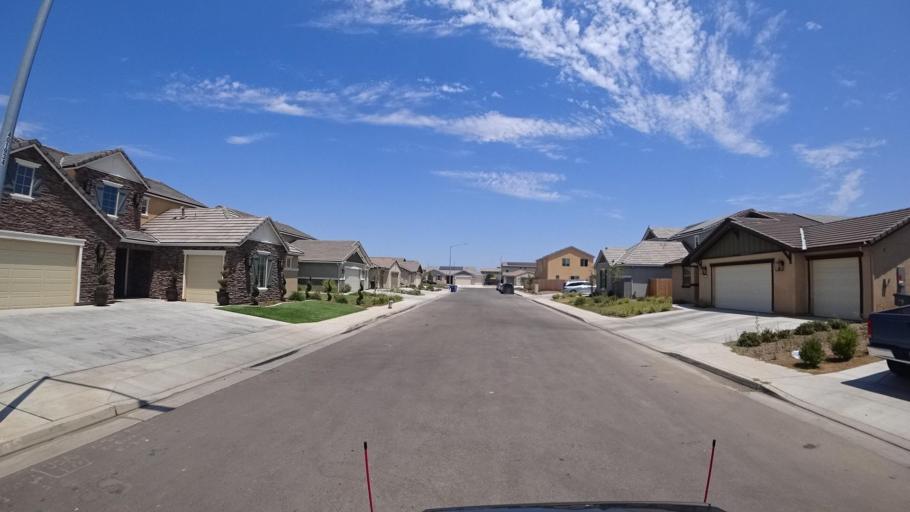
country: US
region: California
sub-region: Fresno County
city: Tarpey Village
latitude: 36.7779
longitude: -119.6591
